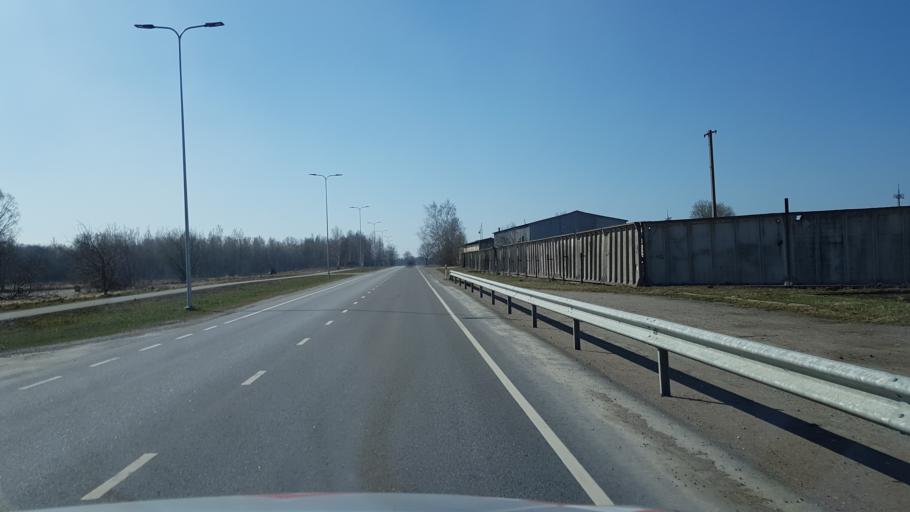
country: EE
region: Ida-Virumaa
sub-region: Kohtla-Jaerve linn
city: Kohtla-Jarve
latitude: 59.3730
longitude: 27.2537
